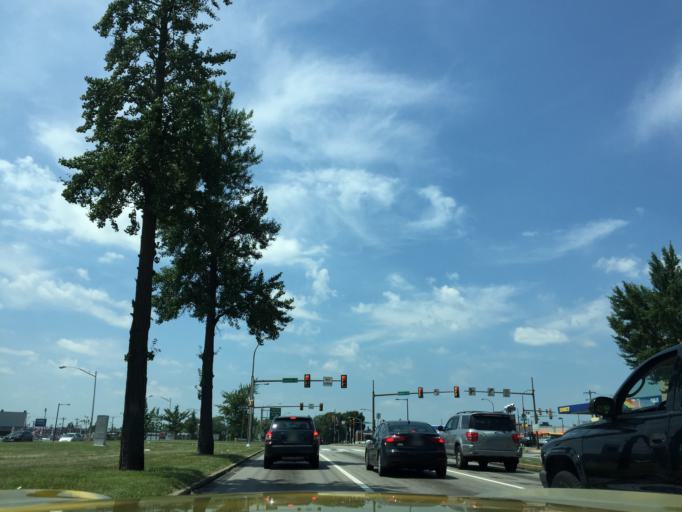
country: US
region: New Jersey
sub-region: Burlington County
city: Palmyra
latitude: 40.0355
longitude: -75.0691
